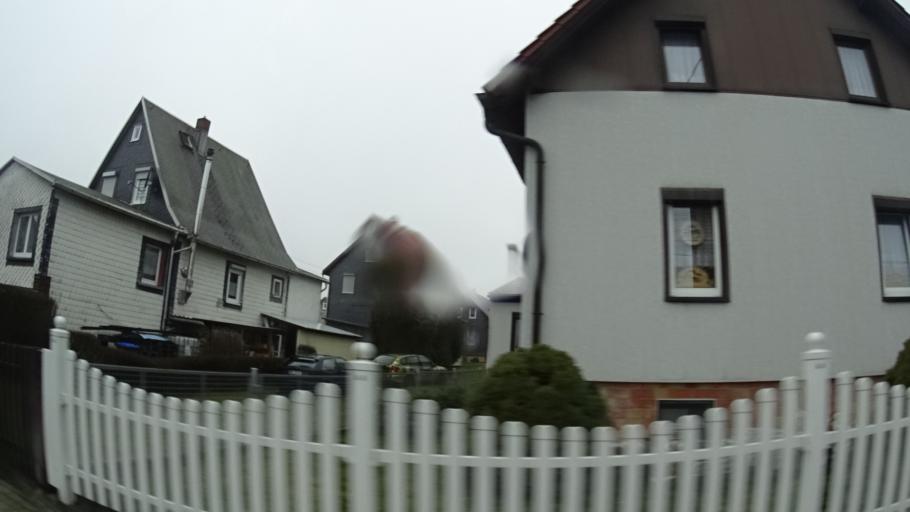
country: DE
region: Thuringia
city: Eisfeld
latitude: 50.4969
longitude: 10.9025
